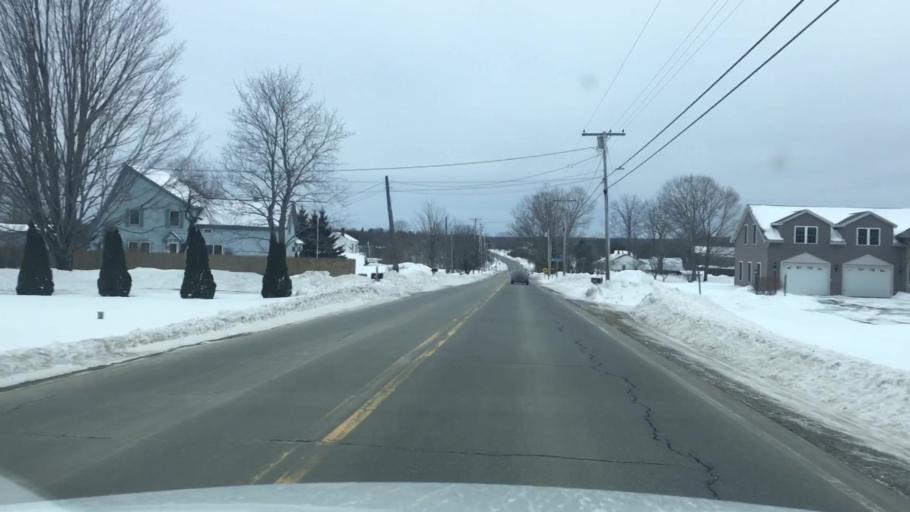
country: US
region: Maine
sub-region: Penobscot County
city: Charleston
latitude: 44.9957
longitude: -69.0476
